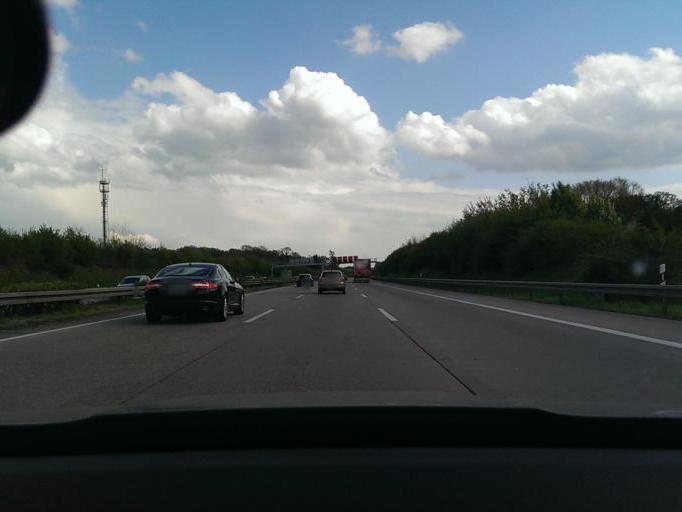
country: DE
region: Lower Saxony
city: Isernhagen Farster Bauerschaft
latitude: 52.4795
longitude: 9.8493
